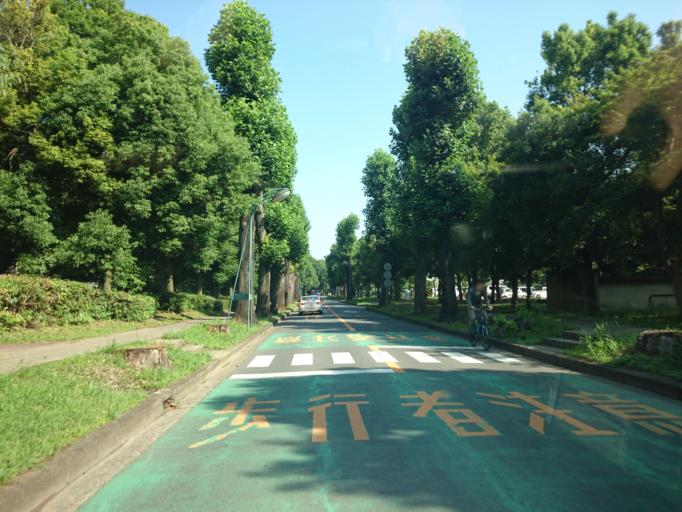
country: JP
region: Ibaraki
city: Naka
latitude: 36.0944
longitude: 140.1035
